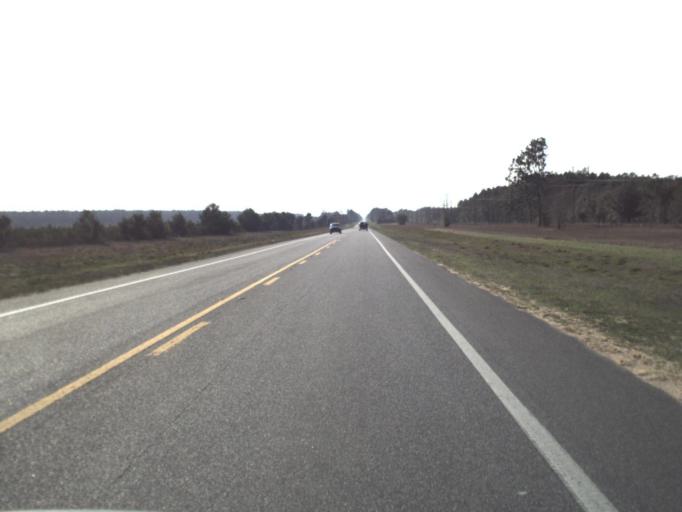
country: US
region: Florida
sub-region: Bay County
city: Lynn Haven
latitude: 30.4389
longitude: -85.7063
